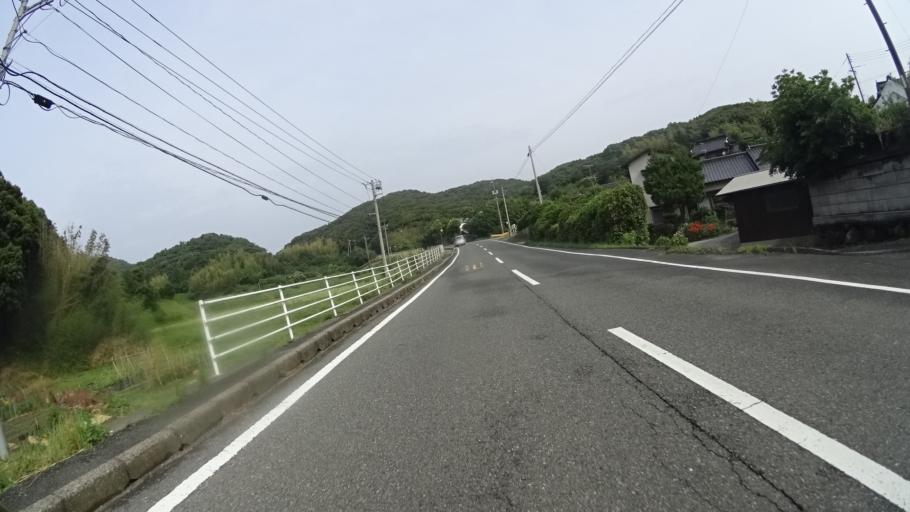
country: JP
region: Yamaguchi
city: Shimonoseki
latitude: 34.0831
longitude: 130.8898
